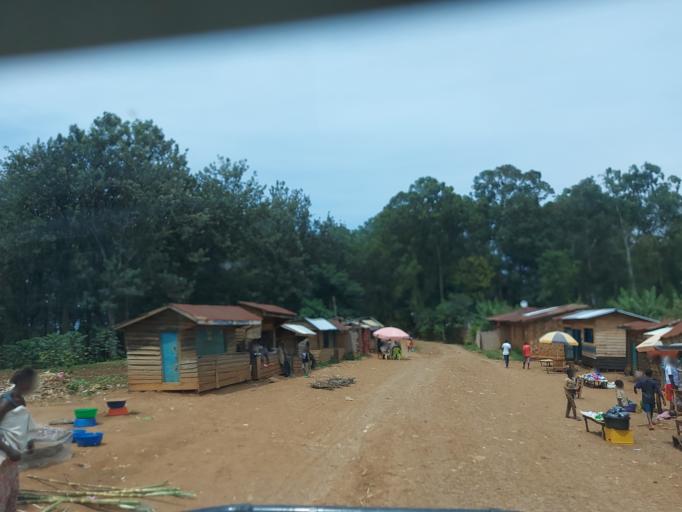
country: RW
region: Western Province
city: Cyangugu
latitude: -2.2349
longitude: 28.8568
